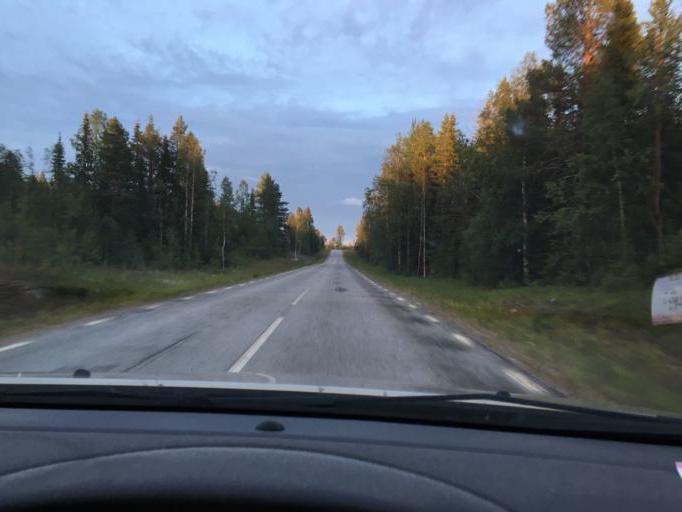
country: SE
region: Norrbotten
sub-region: Lulea Kommun
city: Ranea
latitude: 66.0516
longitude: 22.3863
